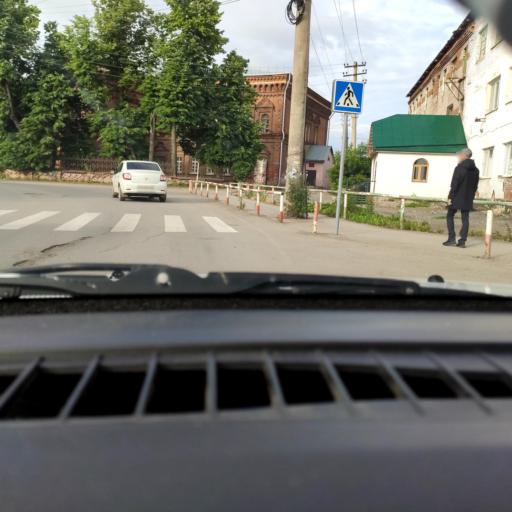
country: RU
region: Perm
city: Kungur
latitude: 57.4238
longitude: 56.9539
